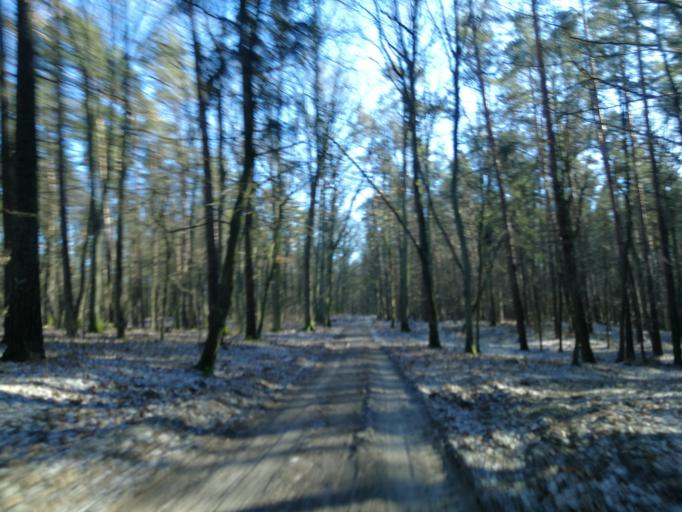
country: PL
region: Kujawsko-Pomorskie
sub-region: Powiat brodnicki
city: Gorzno
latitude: 53.2138
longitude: 19.6760
